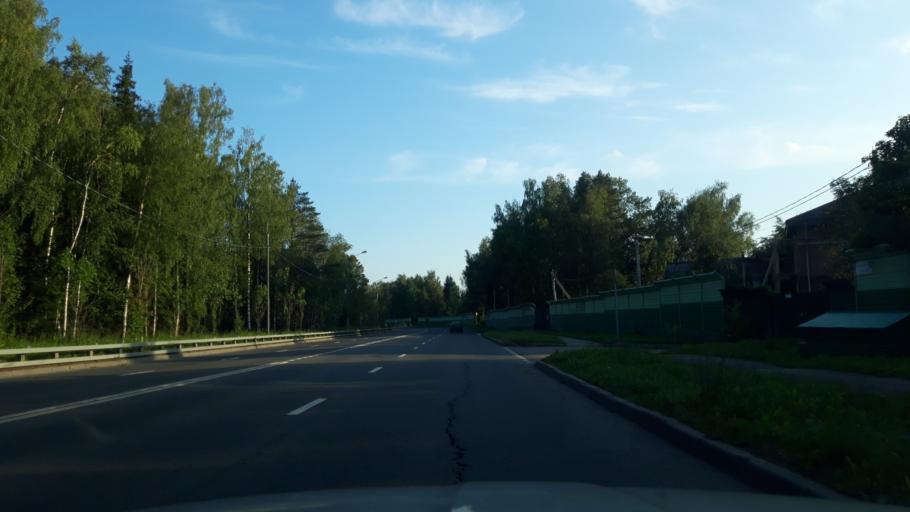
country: RU
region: Moskovskaya
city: Alabushevo
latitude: 56.0041
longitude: 37.1650
